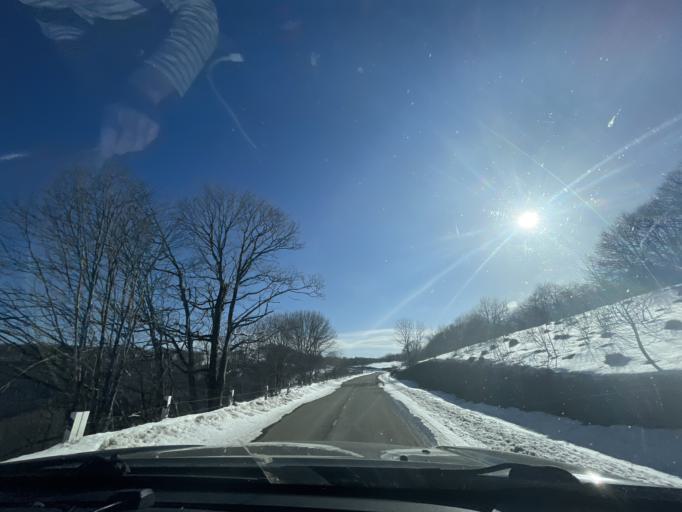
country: GE
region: Kvemo Kartli
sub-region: Tetri Tsqaro
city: Manglisi
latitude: 41.7673
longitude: 44.5072
